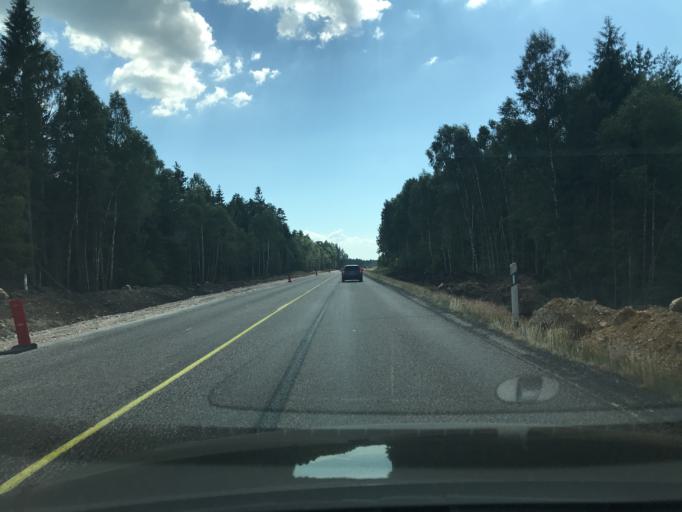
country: SE
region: Kronoberg
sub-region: Almhults Kommun
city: AElmhult
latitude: 56.5551
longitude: 14.1741
